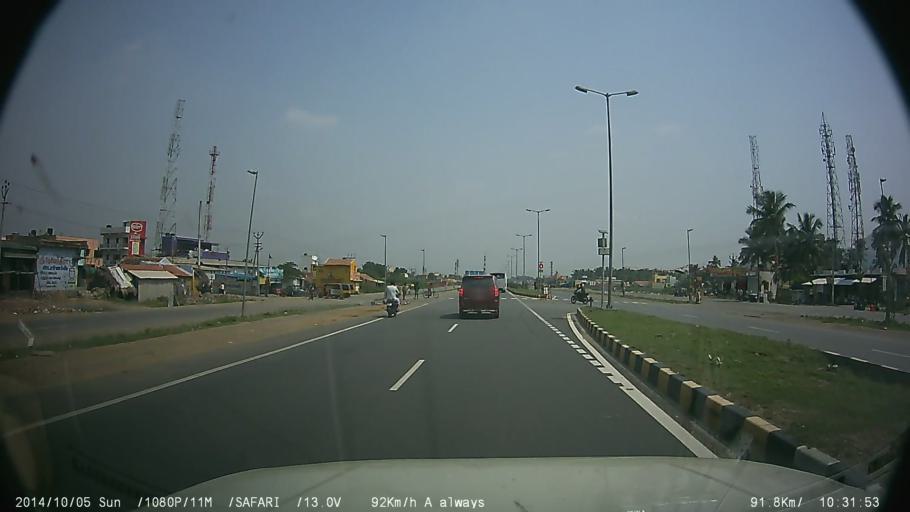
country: IN
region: Tamil Nadu
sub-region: Salem
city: Salem
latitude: 11.6314
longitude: 78.1672
